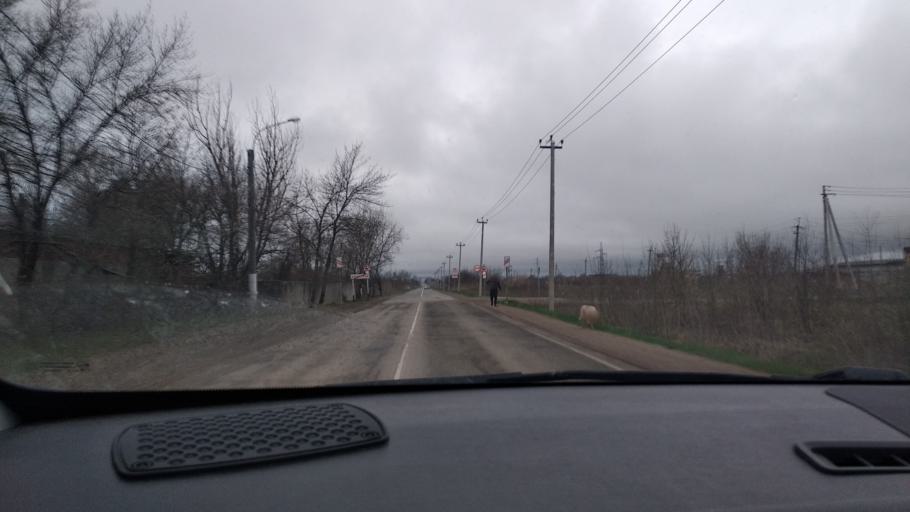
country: RU
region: Krasnodarskiy
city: Afipskiy
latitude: 44.8947
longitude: 38.8220
